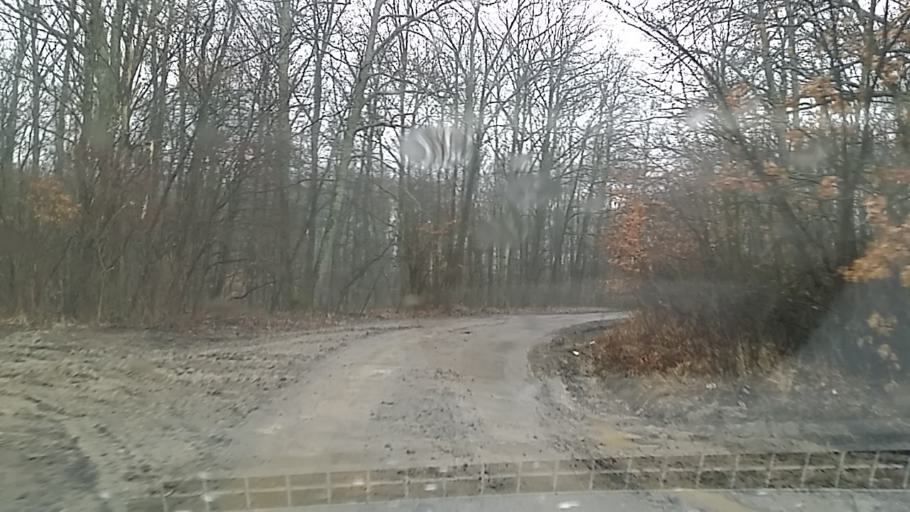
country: HU
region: Borsod-Abauj-Zemplen
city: Rudabanya
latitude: 48.4173
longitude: 20.5766
